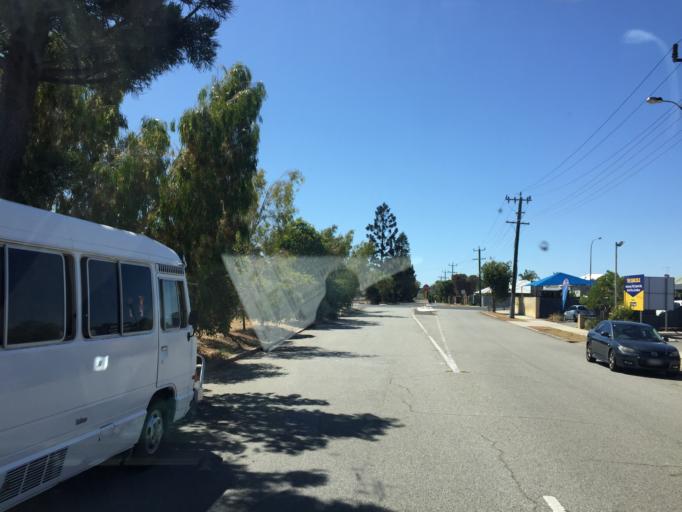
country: AU
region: Western Australia
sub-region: Victoria Park
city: Victoria Park
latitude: -31.9799
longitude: 115.9105
